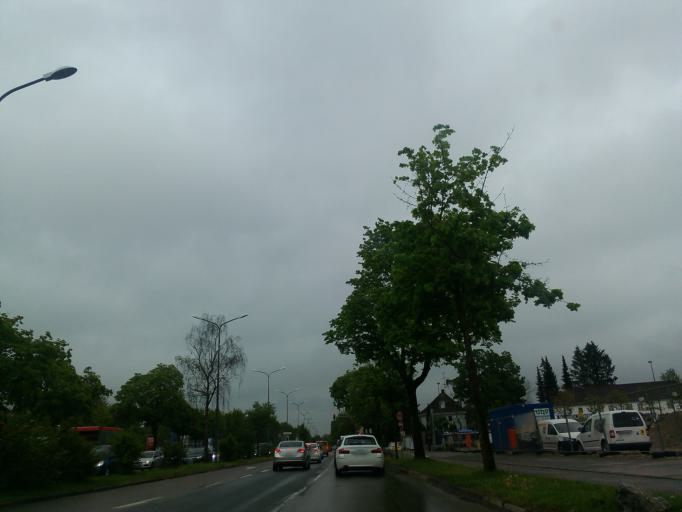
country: DE
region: Bavaria
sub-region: Upper Bavaria
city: Neubiberg
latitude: 48.1218
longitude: 11.6633
